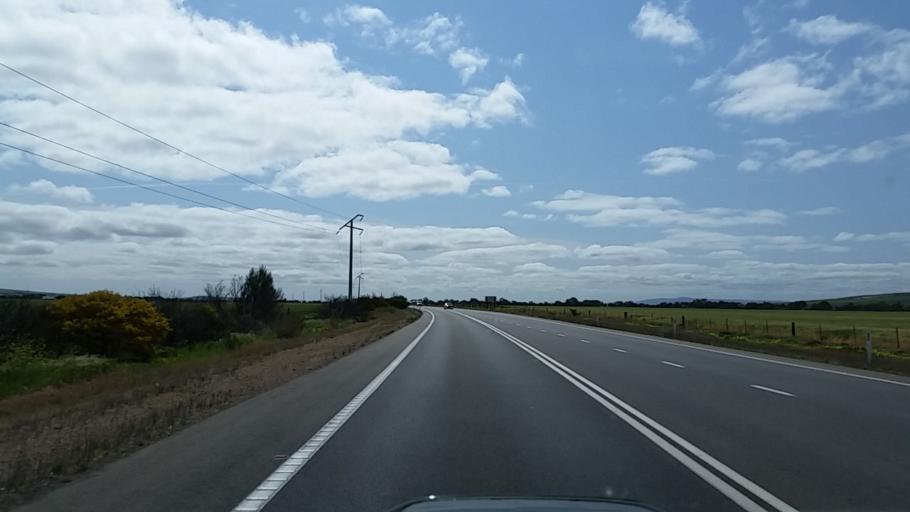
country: AU
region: South Australia
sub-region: Port Pirie City and Dists
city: Crystal Brook
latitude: -33.4932
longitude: 138.1808
